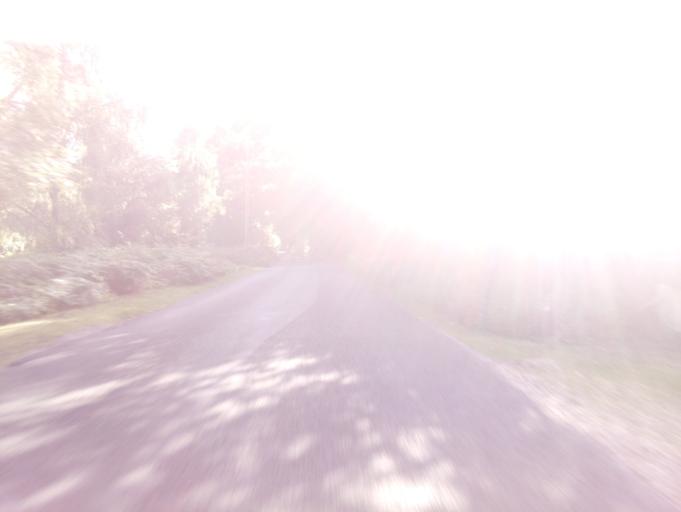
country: GB
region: England
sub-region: Hampshire
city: West Wellow
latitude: 50.9624
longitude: -1.5719
